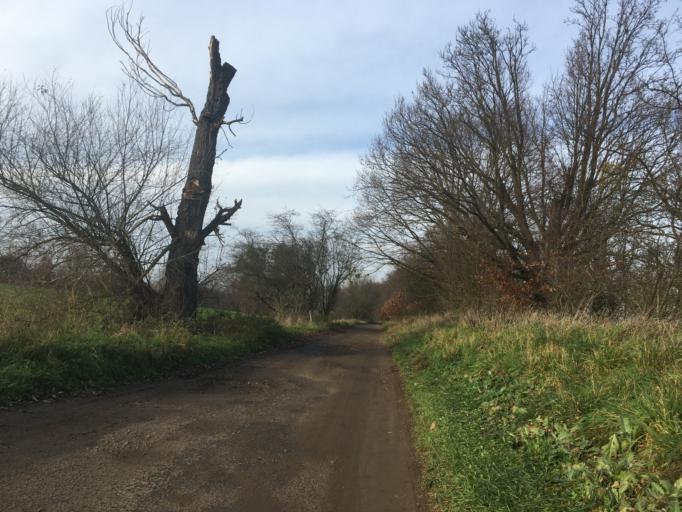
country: DE
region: Brandenburg
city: Bad Freienwalde
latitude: 52.8193
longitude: 14.0014
